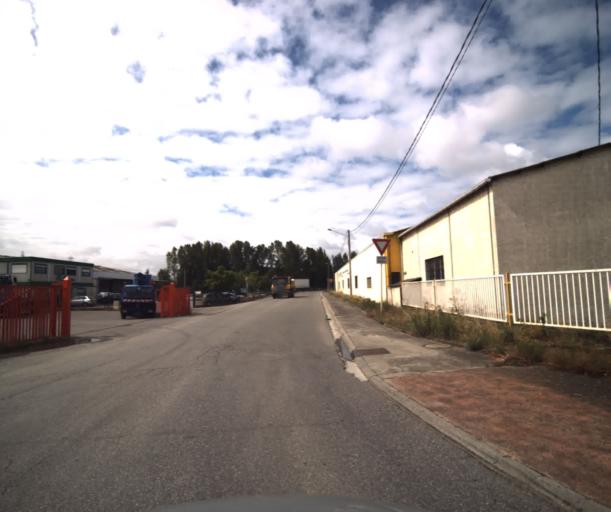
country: FR
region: Midi-Pyrenees
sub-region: Departement de la Haute-Garonne
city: Pinsaguel
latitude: 43.5270
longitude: 1.3781
